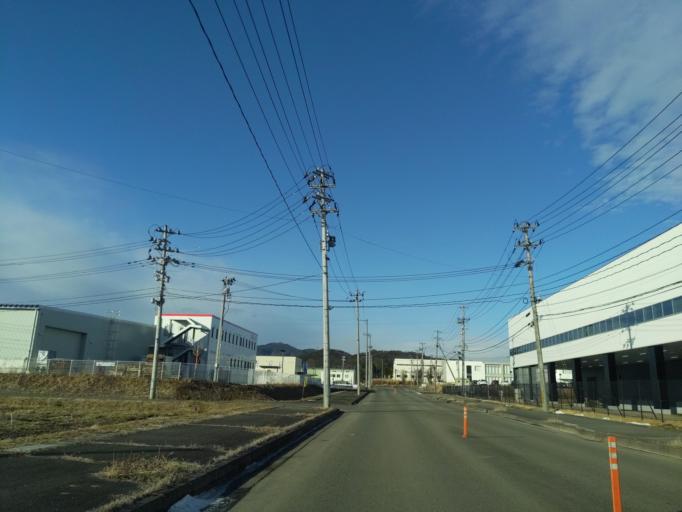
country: JP
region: Fukushima
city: Motomiya
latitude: 37.4763
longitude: 140.3701
